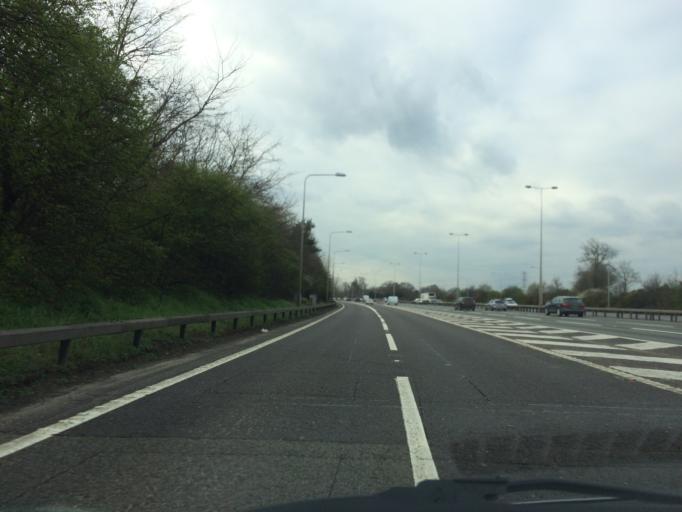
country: GB
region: England
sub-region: Surrey
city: Chertsey
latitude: 51.3781
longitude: -0.5115
